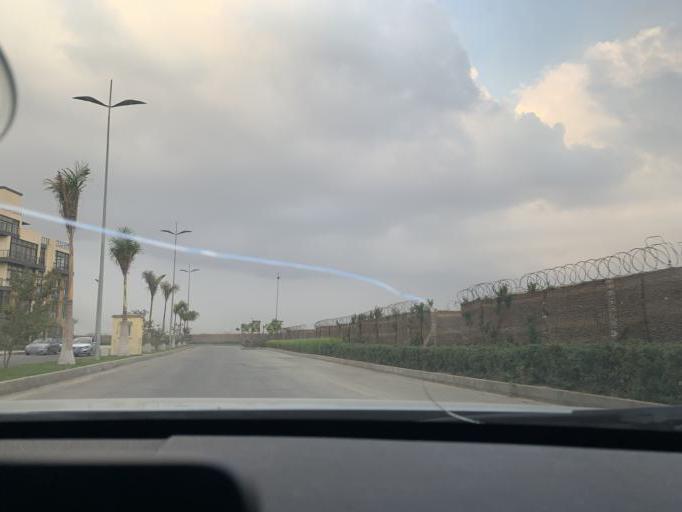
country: EG
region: Muhafazat al Qalyubiyah
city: Al Khankah
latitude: 30.0975
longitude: 31.6587
